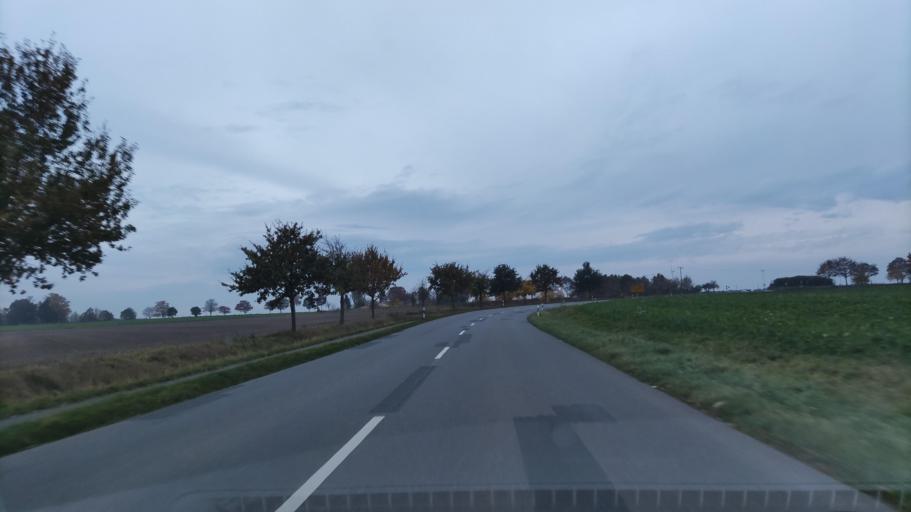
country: DE
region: Lower Saxony
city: Tulau
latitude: 52.6448
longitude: 10.8727
